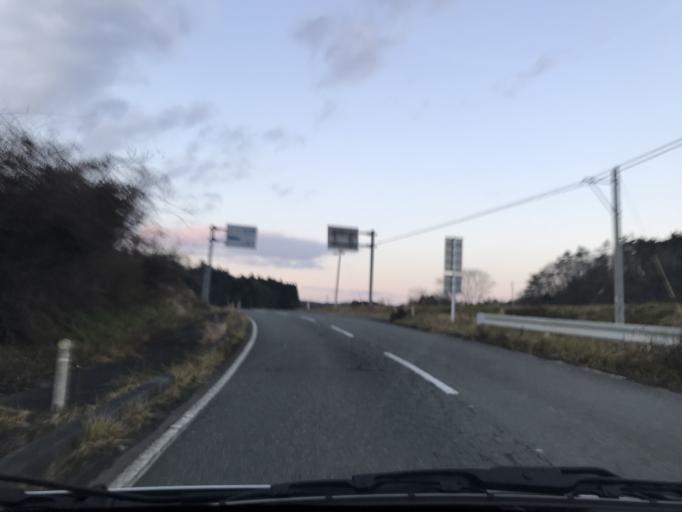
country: JP
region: Iwate
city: Ichinoseki
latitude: 38.8242
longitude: 141.1182
